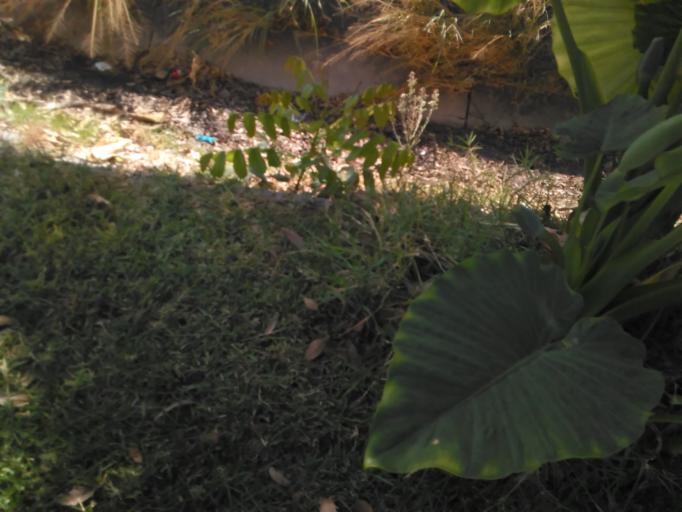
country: MX
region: Nayarit
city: Tepic
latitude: 21.4954
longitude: -104.8878
